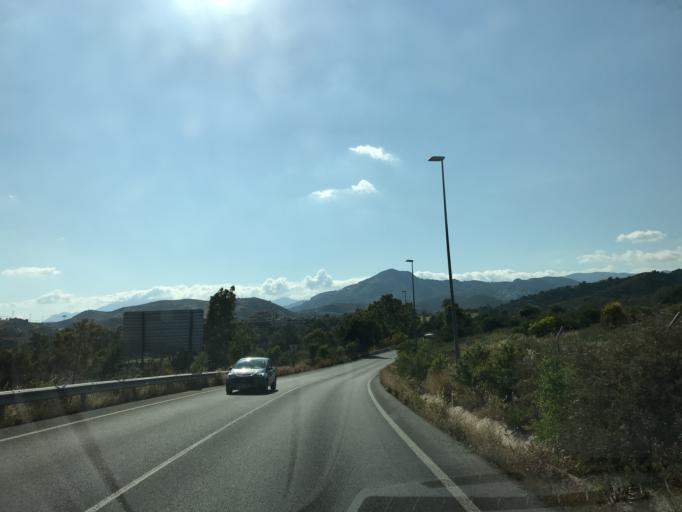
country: ES
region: Andalusia
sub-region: Provincia de Malaga
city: Benahavis
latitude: 36.5002
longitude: -5.0124
